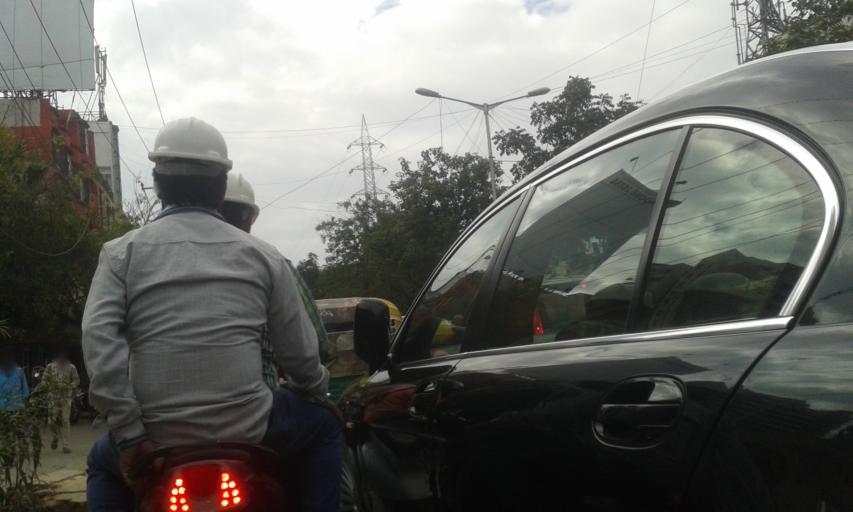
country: IN
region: Karnataka
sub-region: Bangalore Urban
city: Bangalore
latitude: 12.9064
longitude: 77.5751
